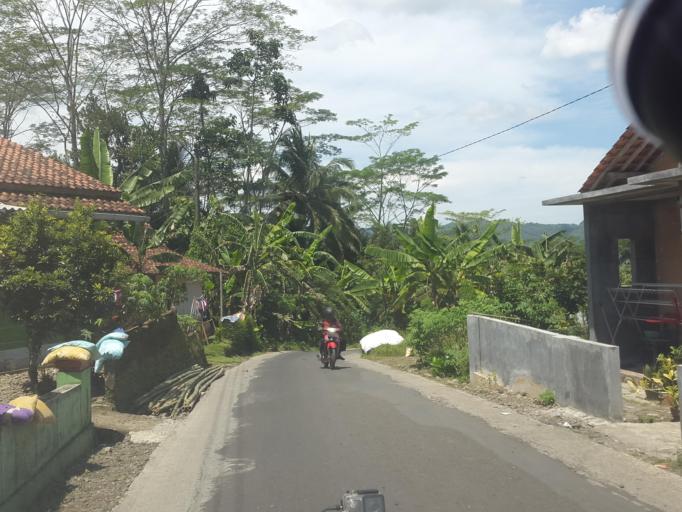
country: ID
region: Central Java
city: Sangkalputung
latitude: -7.4104
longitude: 109.0586
